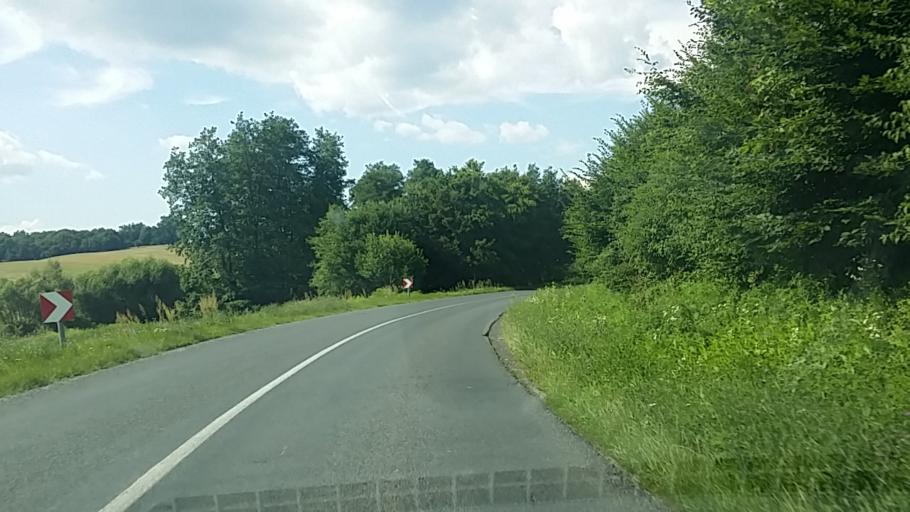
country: HU
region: Zala
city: Becsehely
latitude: 46.4794
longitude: 16.7915
